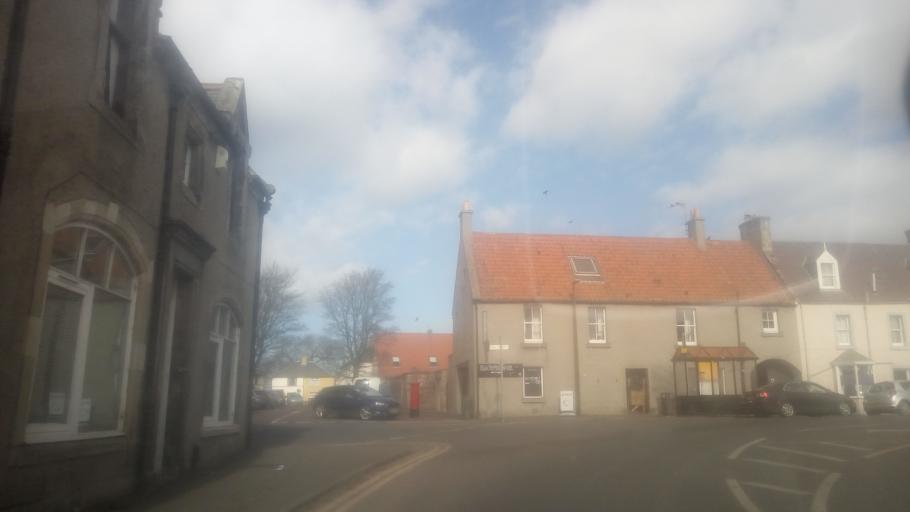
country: GB
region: Scotland
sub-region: East Lothian
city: Ormiston
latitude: 55.9127
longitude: -2.9401
